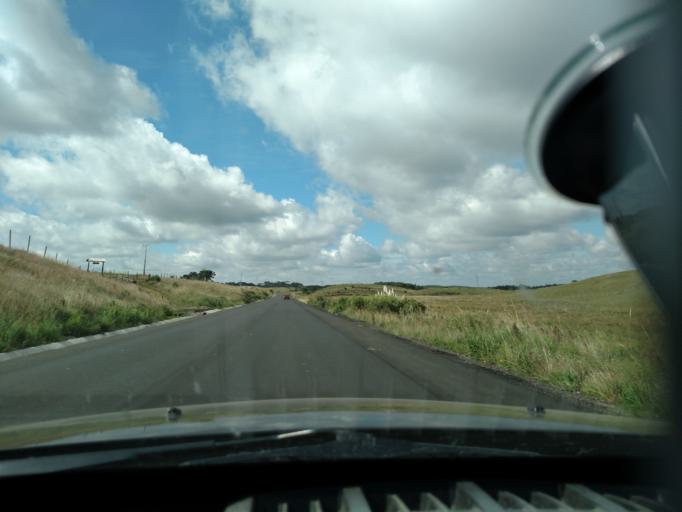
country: BR
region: Santa Catarina
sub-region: Lages
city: Lages
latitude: -28.0123
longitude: -50.0853
